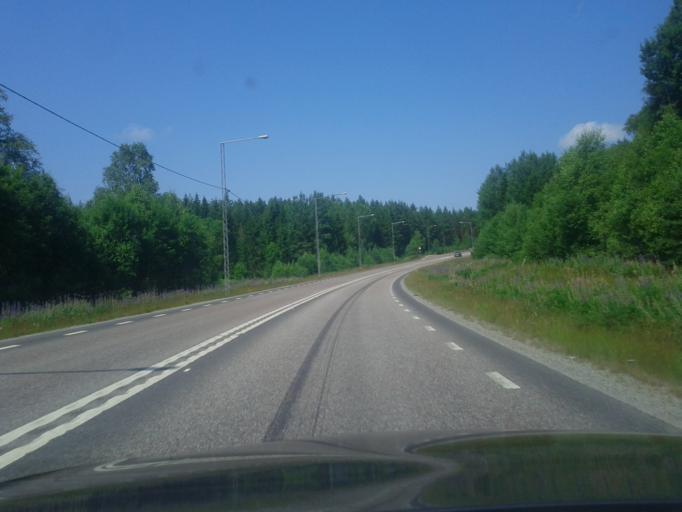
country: SE
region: Stockholm
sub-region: Vallentuna Kommun
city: Vallentuna
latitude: 59.4965
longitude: 18.1026
